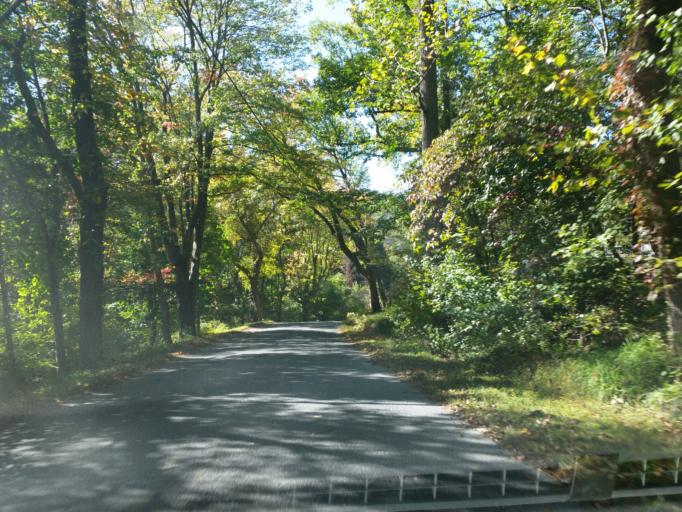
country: US
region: Pennsylvania
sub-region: Lebanon County
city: Jonestown
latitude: 40.4761
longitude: -76.5159
